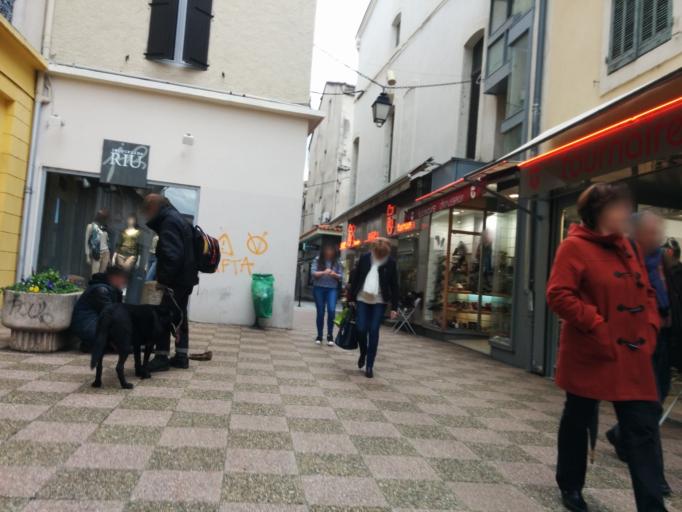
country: FR
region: Languedoc-Roussillon
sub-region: Departement du Gard
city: Ales
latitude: 44.1225
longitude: 4.0802
